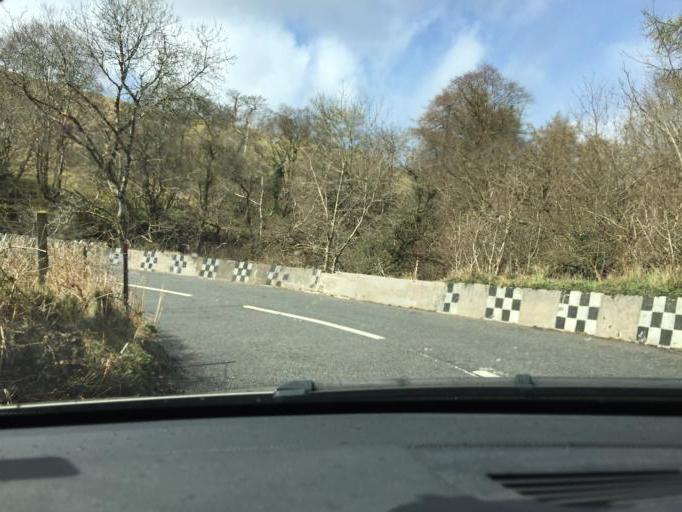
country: GB
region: Northern Ireland
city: Cushendall
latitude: 55.1283
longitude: -6.0858
